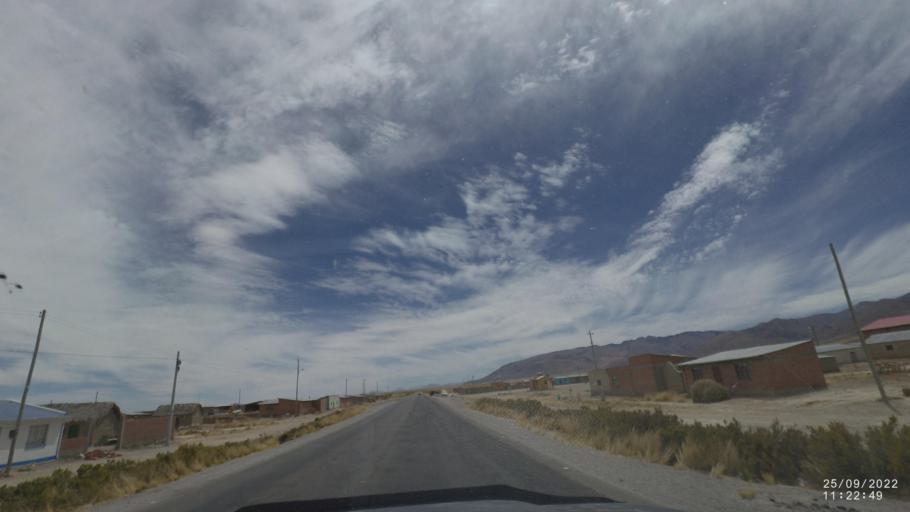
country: BO
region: Oruro
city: Challapata
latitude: -19.1198
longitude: -66.7694
